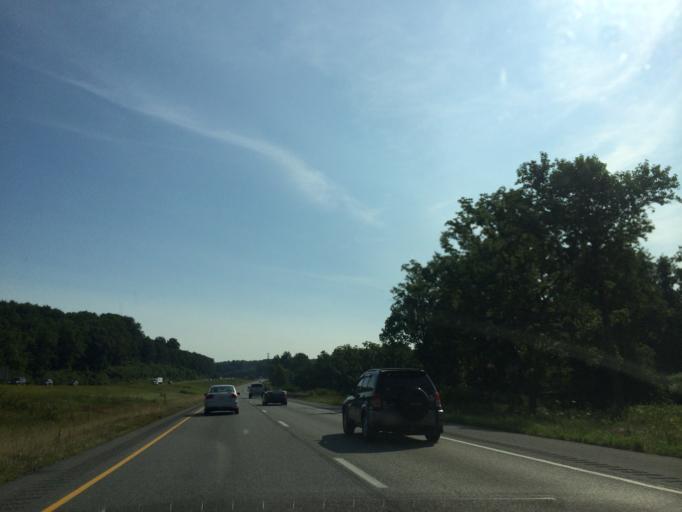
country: US
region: Pennsylvania
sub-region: Lancaster County
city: Reamstown
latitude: 40.1774
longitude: -76.1389
